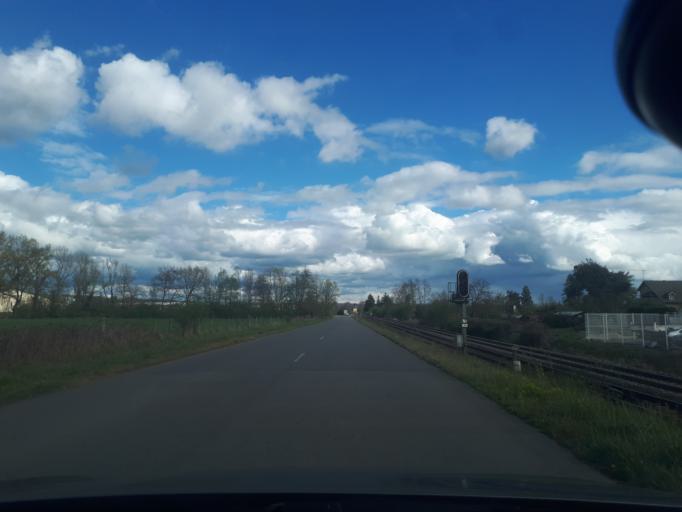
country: FR
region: Rhone-Alpes
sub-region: Departement de la Loire
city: Balbigny
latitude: 45.8248
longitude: 4.1783
